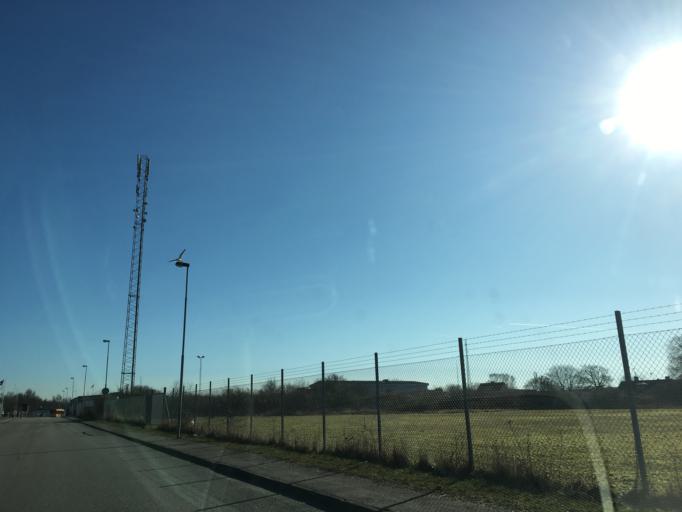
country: SE
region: Skane
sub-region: Lomma Kommun
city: Lomma
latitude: 55.6816
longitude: 13.0843
